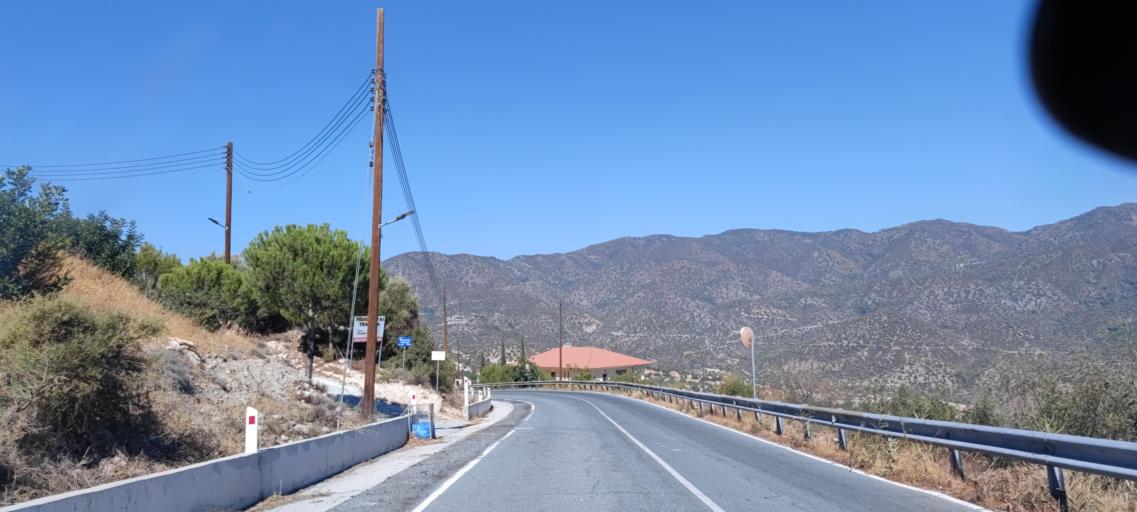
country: CY
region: Limassol
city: Mouttagiaka
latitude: 34.7667
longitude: 33.0574
